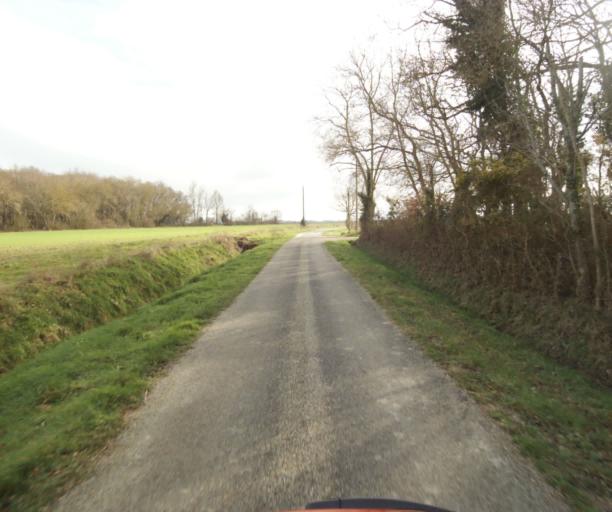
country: FR
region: Midi-Pyrenees
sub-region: Departement de l'Ariege
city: Mazeres
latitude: 43.2061
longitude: 1.6804
